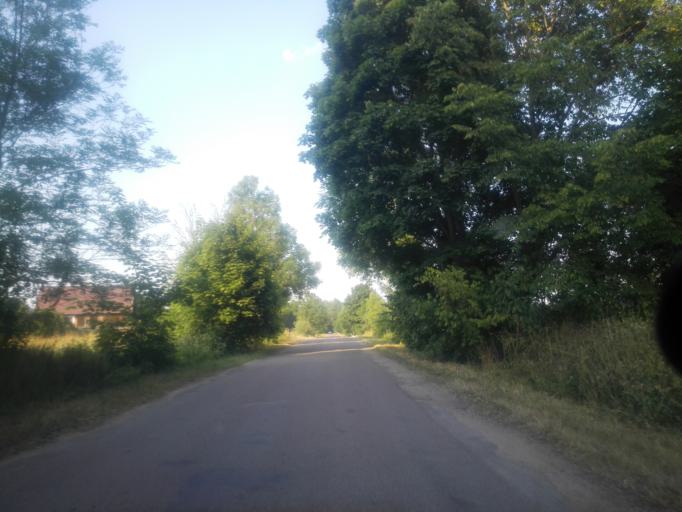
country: PL
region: Podlasie
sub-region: Suwalki
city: Suwalki
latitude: 54.0679
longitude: 22.9935
